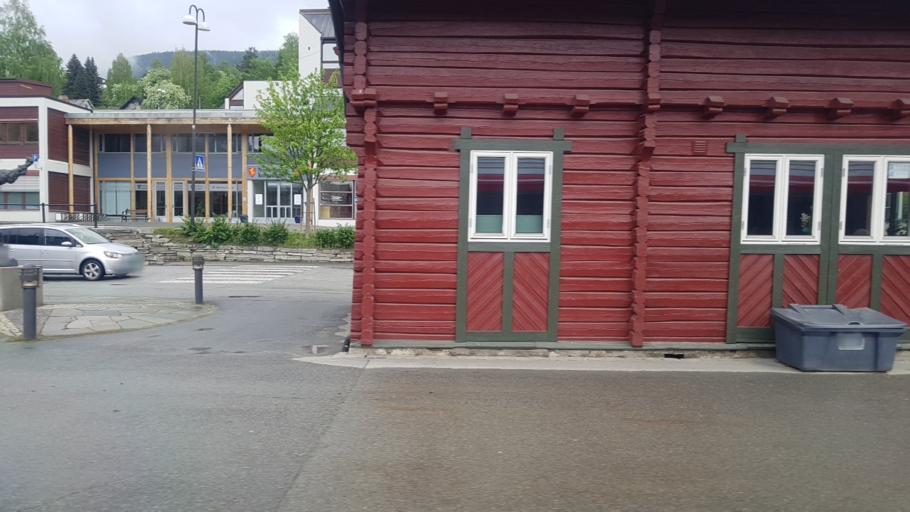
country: NO
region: Oppland
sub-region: Nord-Fron
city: Vinstra
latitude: 61.5990
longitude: 9.7341
